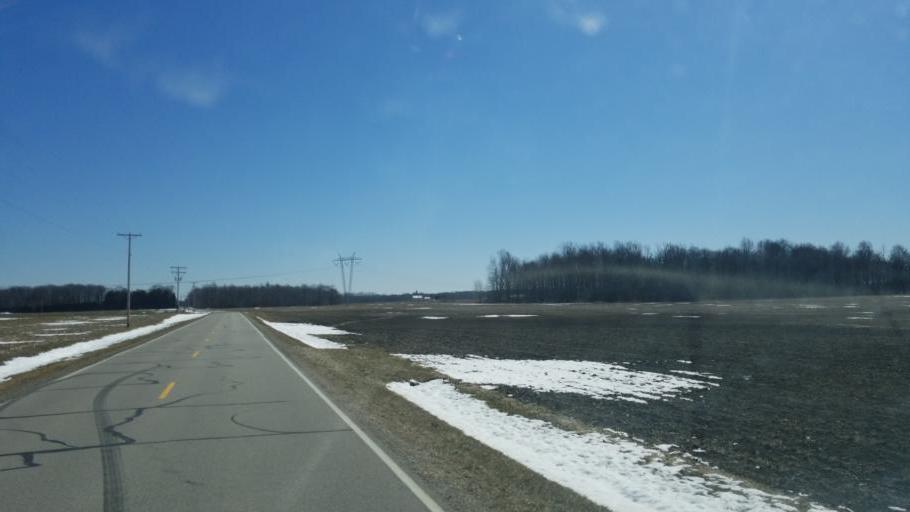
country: US
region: Ohio
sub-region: Crawford County
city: Bucyrus
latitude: 40.8047
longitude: -83.0328
